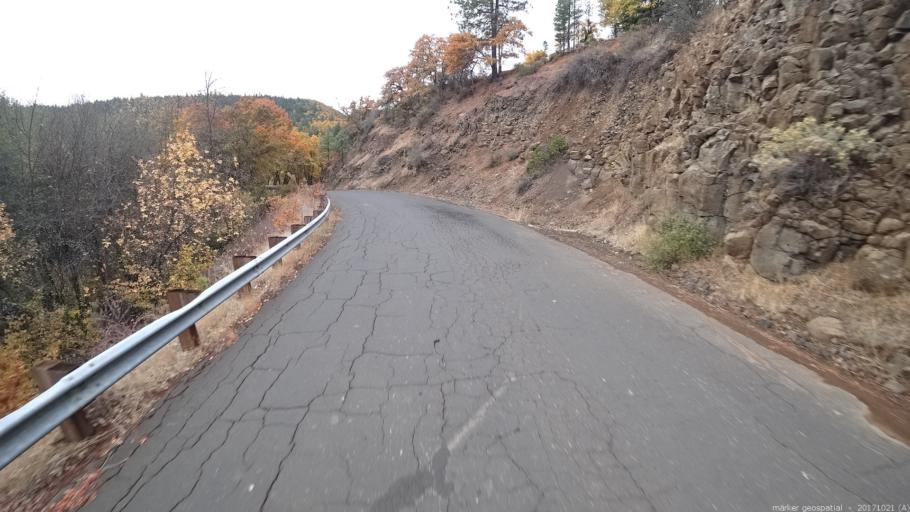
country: US
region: California
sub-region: Shasta County
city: Burney
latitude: 41.0255
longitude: -121.6724
